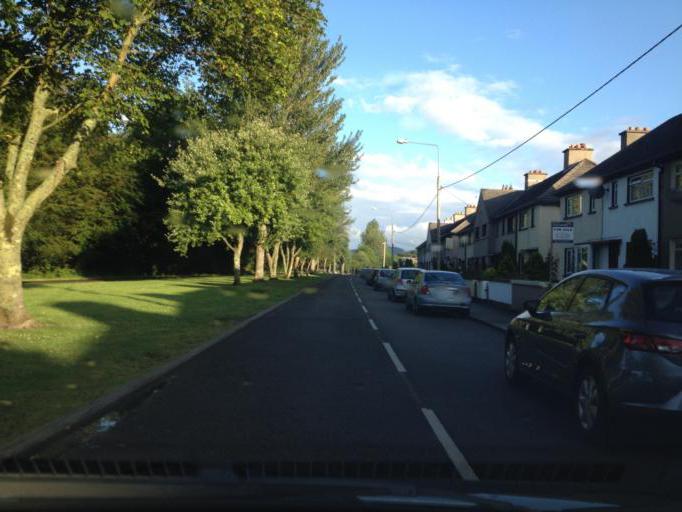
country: IE
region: Connaught
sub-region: Sligo
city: Sligo
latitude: 54.2694
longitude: -8.4570
